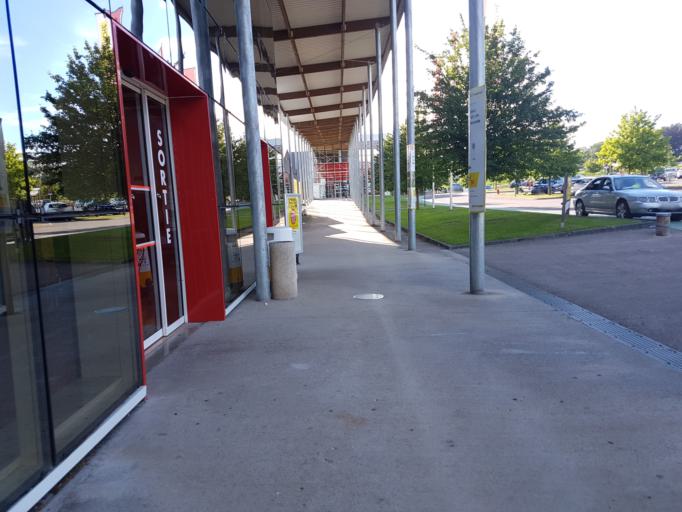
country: FR
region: Franche-Comte
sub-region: Departement de la Haute-Saone
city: Luxeuil-les-Bains
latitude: 47.8098
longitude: 6.3630
